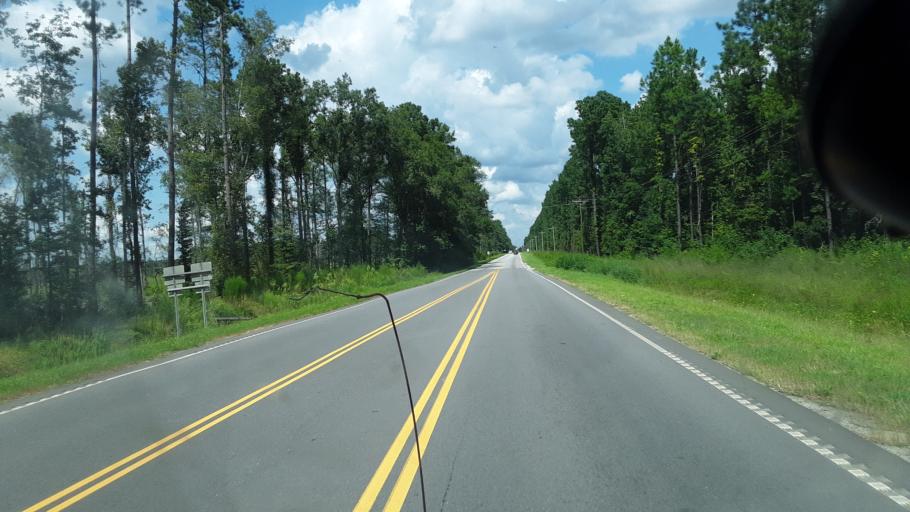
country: US
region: South Carolina
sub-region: Williamsburg County
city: Andrews
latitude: 33.5974
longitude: -79.4421
